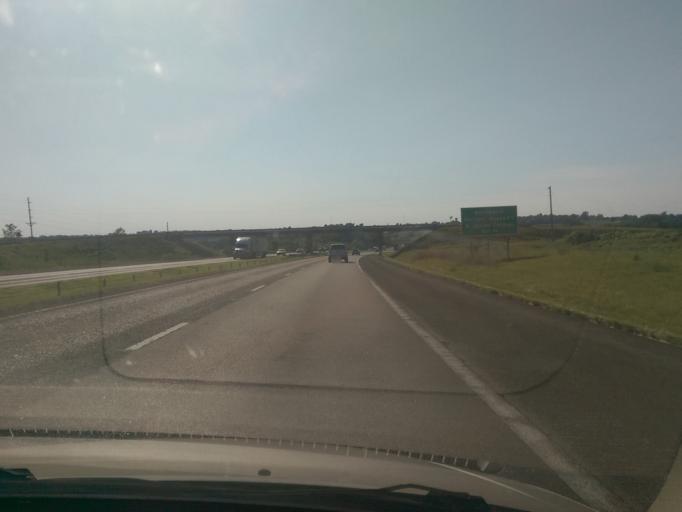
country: US
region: Missouri
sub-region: Lafayette County
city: Higginsville
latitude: 38.9935
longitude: -93.7098
